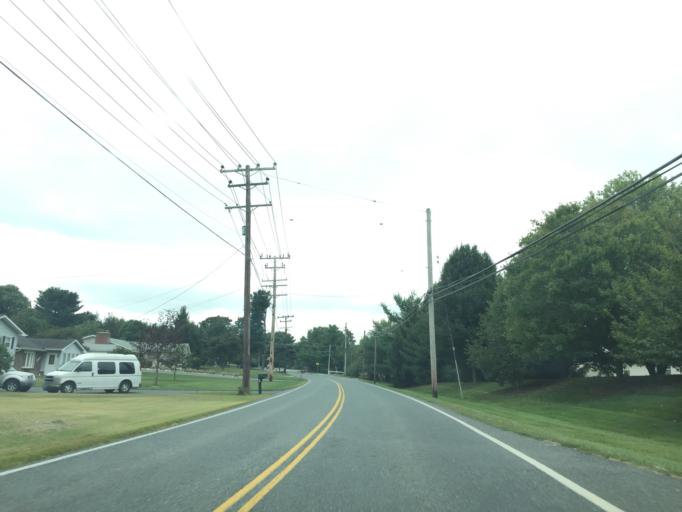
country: US
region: Maryland
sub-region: Harford County
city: Bel Air North
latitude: 39.5770
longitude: -76.3632
